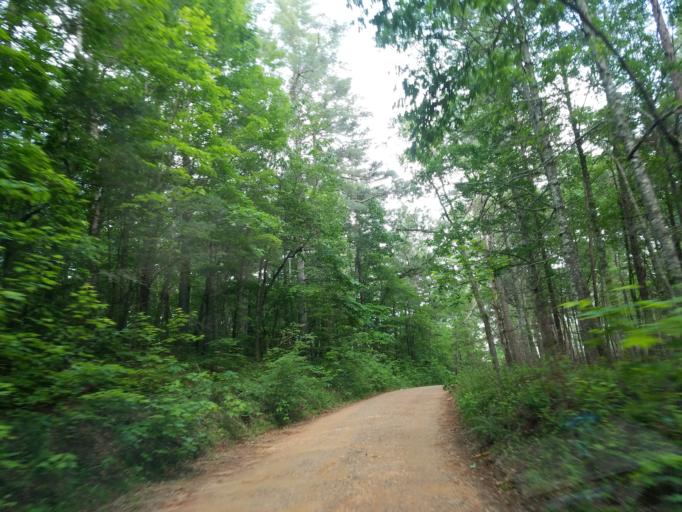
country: US
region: Georgia
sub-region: Lumpkin County
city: Dahlonega
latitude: 34.5830
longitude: -84.1242
